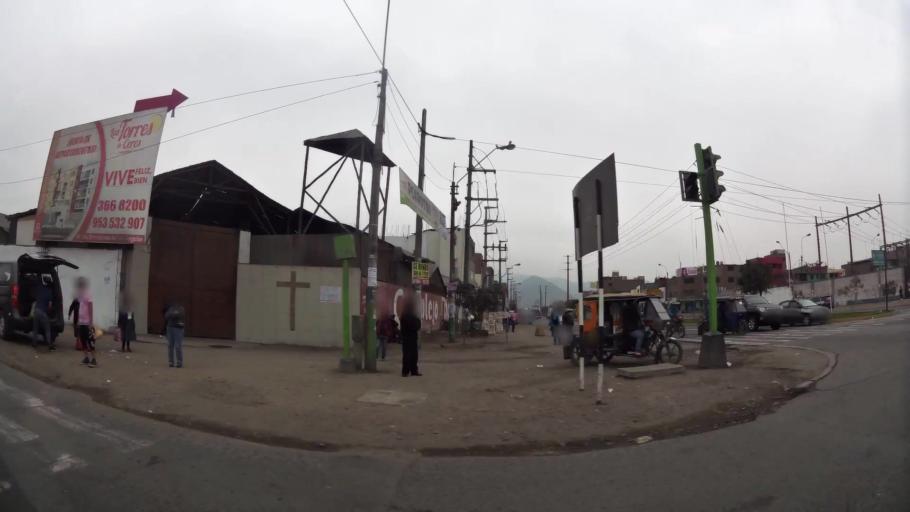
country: PE
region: Lima
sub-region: Lima
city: Vitarte
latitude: -12.0355
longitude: -76.9492
